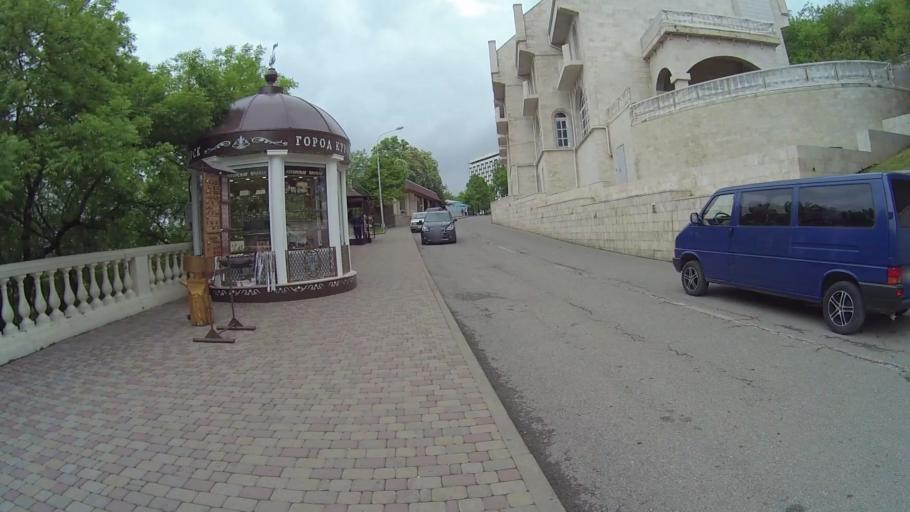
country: RU
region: Stavropol'skiy
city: Goryachevodskiy
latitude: 44.0460
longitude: 43.0994
